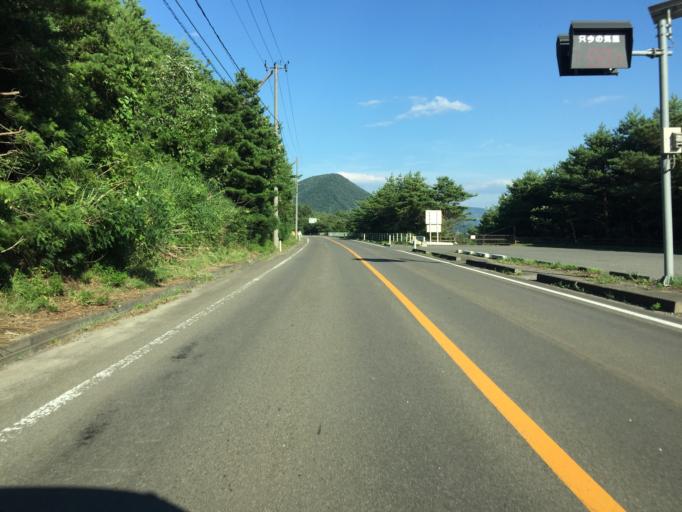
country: JP
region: Miyagi
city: Shiroishi
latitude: 37.9789
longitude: 140.4877
